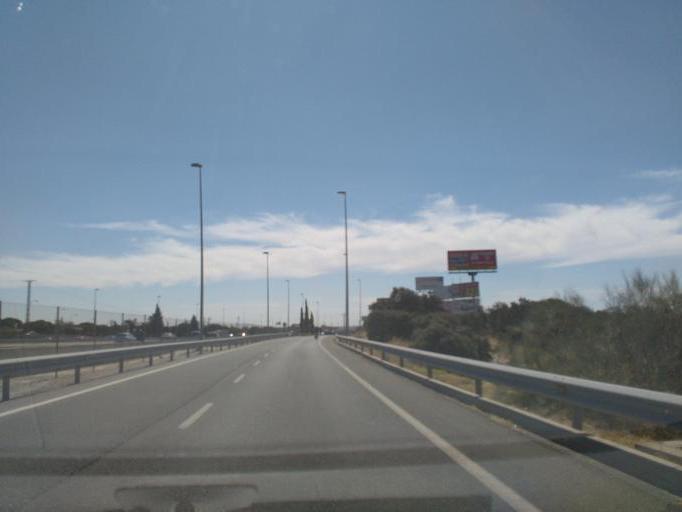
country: ES
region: Madrid
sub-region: Provincia de Madrid
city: Las Matas
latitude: 40.5610
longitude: -3.9031
